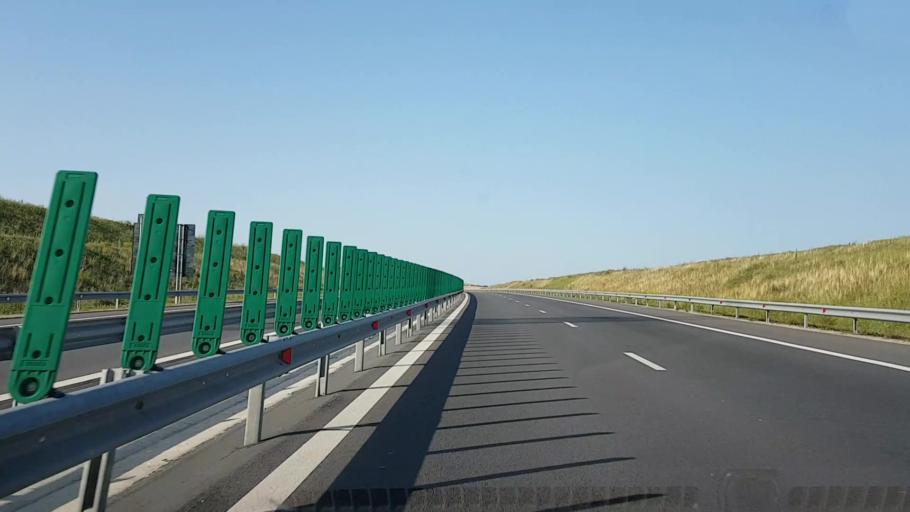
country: RO
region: Alba
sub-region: Comuna Unirea
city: Unirea
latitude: 46.3934
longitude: 23.7883
